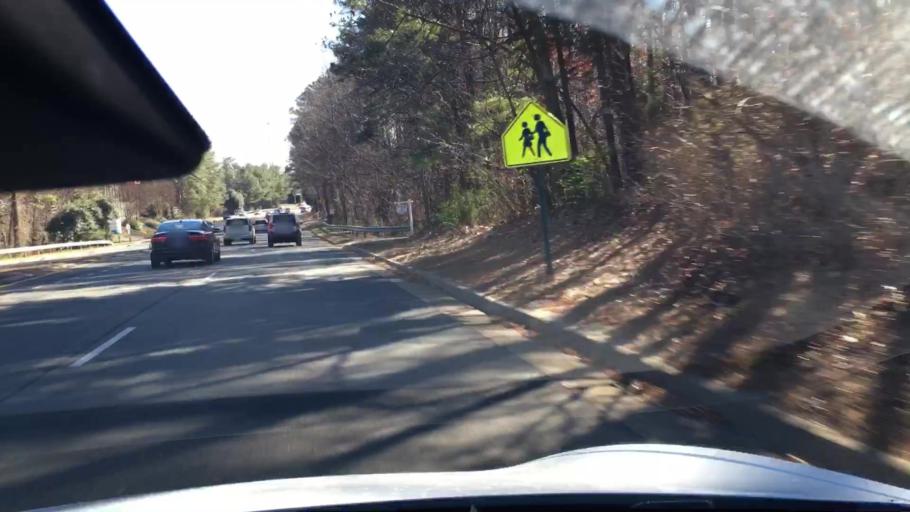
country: US
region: Virginia
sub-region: Henrico County
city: Tuckahoe
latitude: 37.5849
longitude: -77.5706
